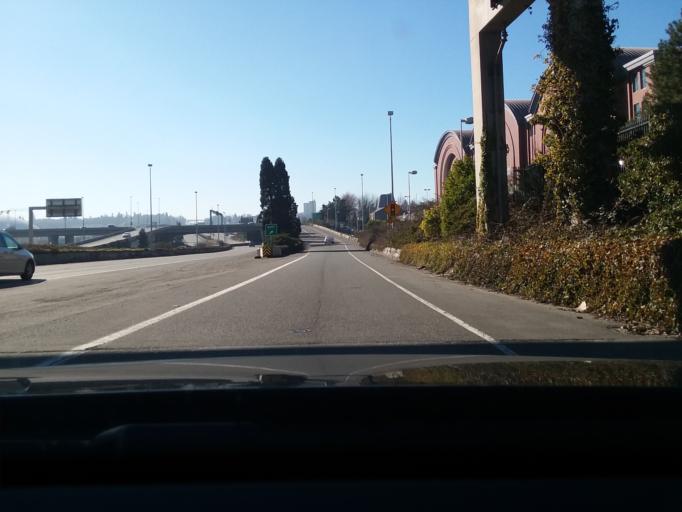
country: US
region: Washington
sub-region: Pierce County
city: Tacoma
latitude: 47.2457
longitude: -122.4355
